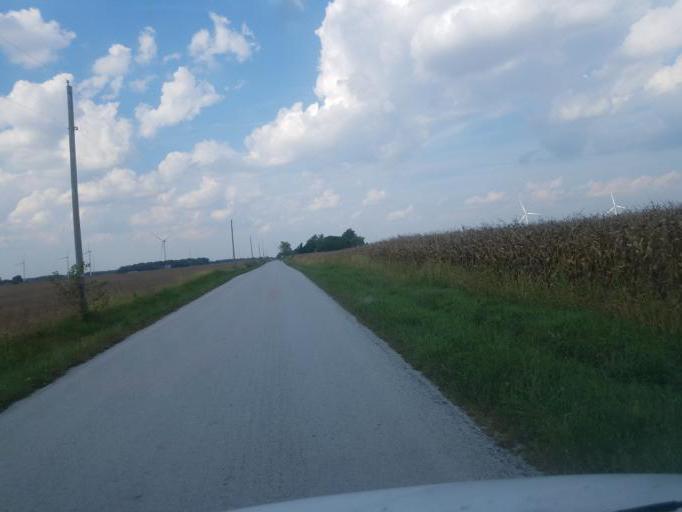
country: US
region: Ohio
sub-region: Hancock County
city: Arlington
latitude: 40.7808
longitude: -83.6710
